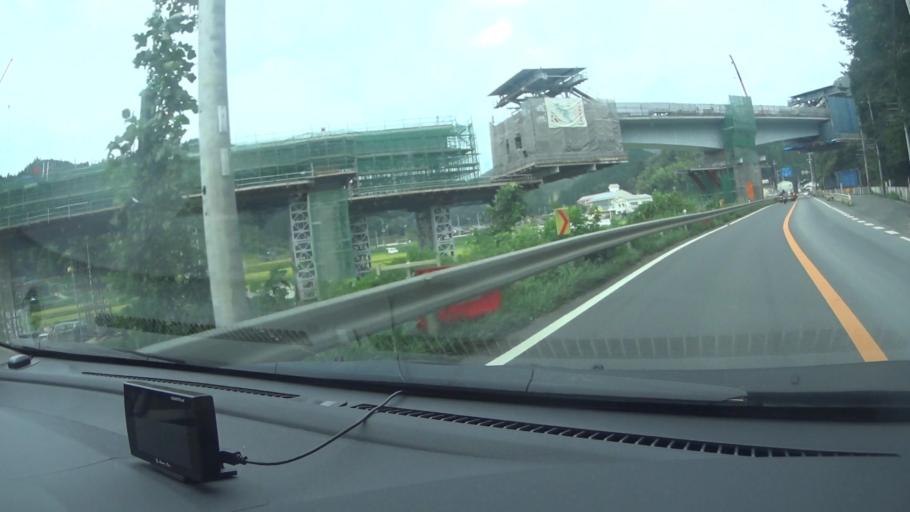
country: JP
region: Kyoto
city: Ayabe
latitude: 35.2184
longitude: 135.3430
